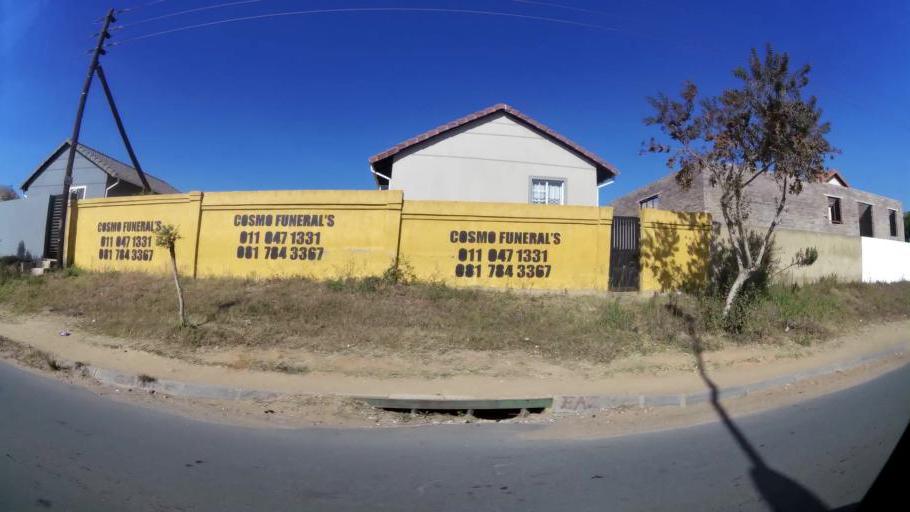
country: ZA
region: Gauteng
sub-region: West Rand District Municipality
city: Muldersdriseloop
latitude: -26.0354
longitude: 27.9246
